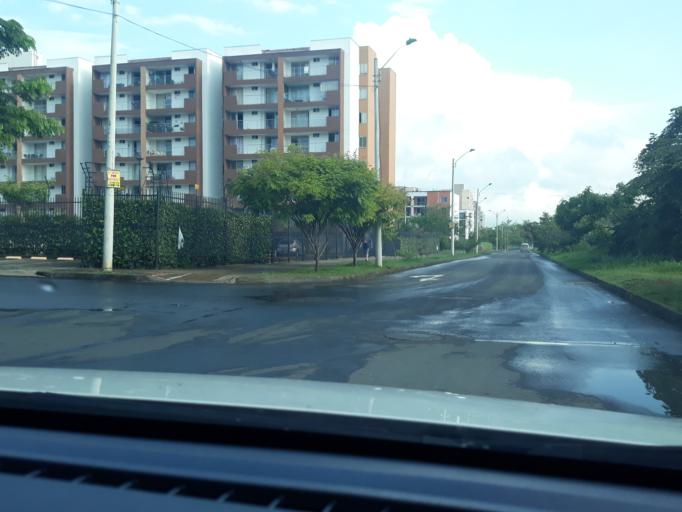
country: CO
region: Valle del Cauca
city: Cali
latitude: 3.3559
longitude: -76.5164
